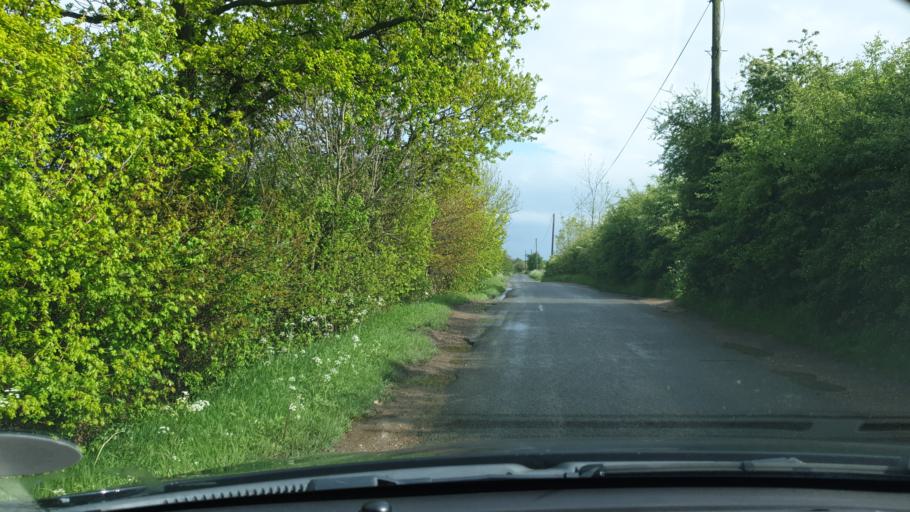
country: GB
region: England
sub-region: Essex
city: Great Bentley
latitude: 51.8387
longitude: 1.0515
